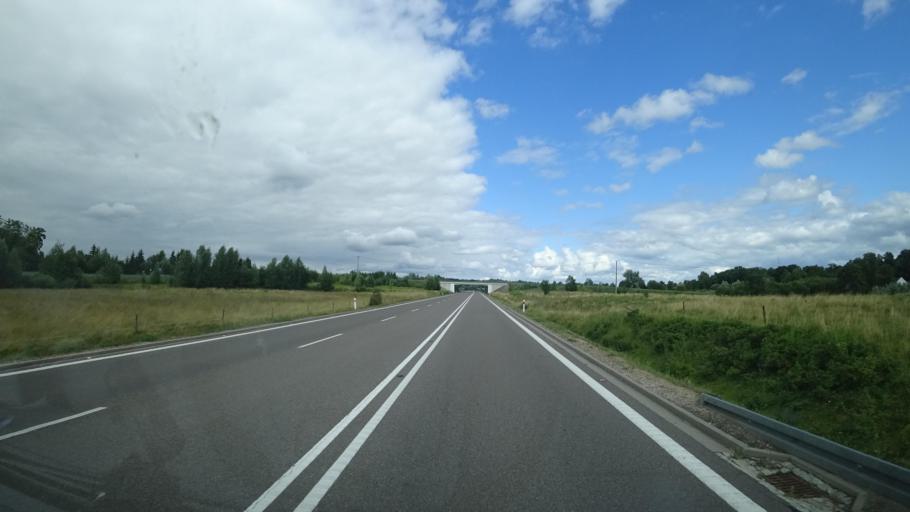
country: PL
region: Warmian-Masurian Voivodeship
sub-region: Powiat goldapski
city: Goldap
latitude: 54.3162
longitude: 22.2869
